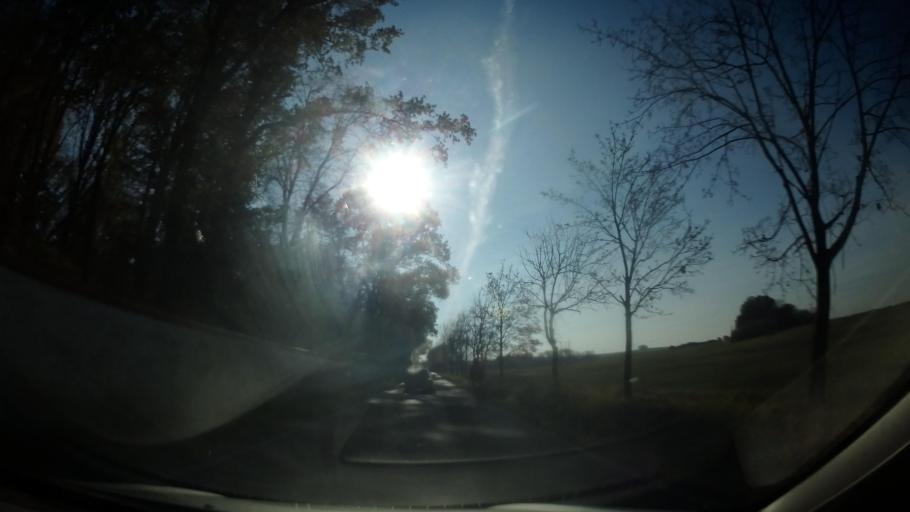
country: CZ
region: Praha
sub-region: Praha 20
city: Horni Pocernice
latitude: 50.0608
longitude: 14.6276
